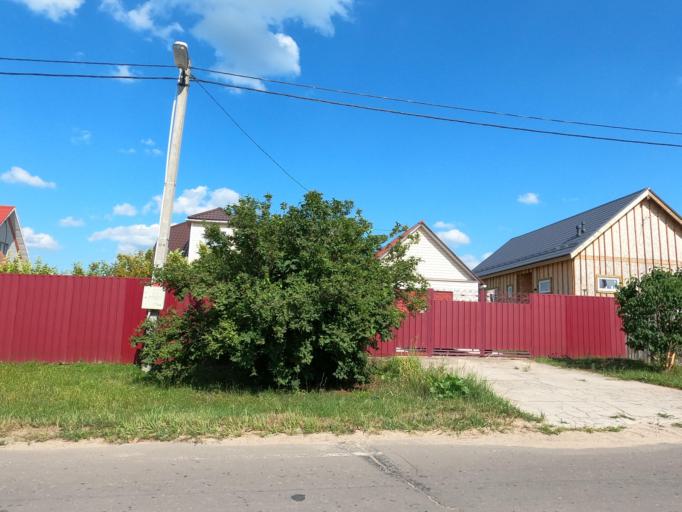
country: RU
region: Moskovskaya
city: Peski
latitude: 55.2277
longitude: 38.7503
